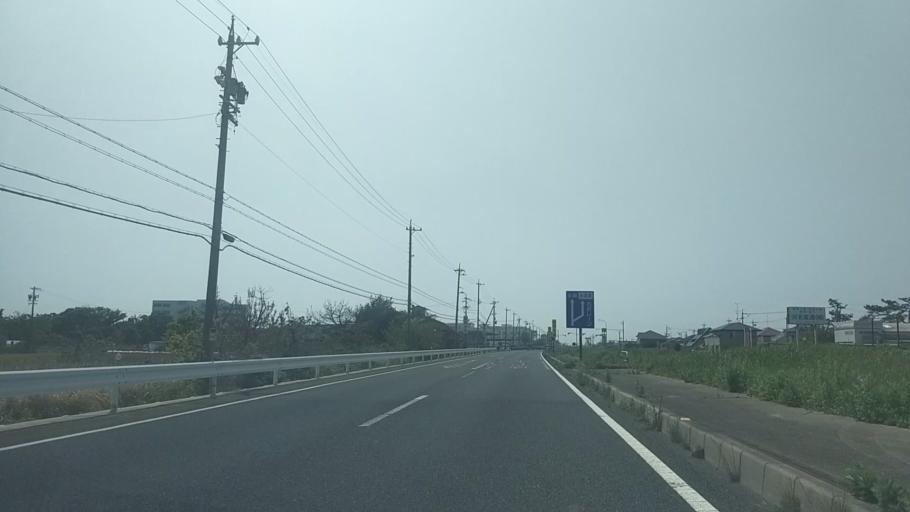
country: JP
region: Shizuoka
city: Hamamatsu
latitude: 34.6703
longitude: 137.7191
